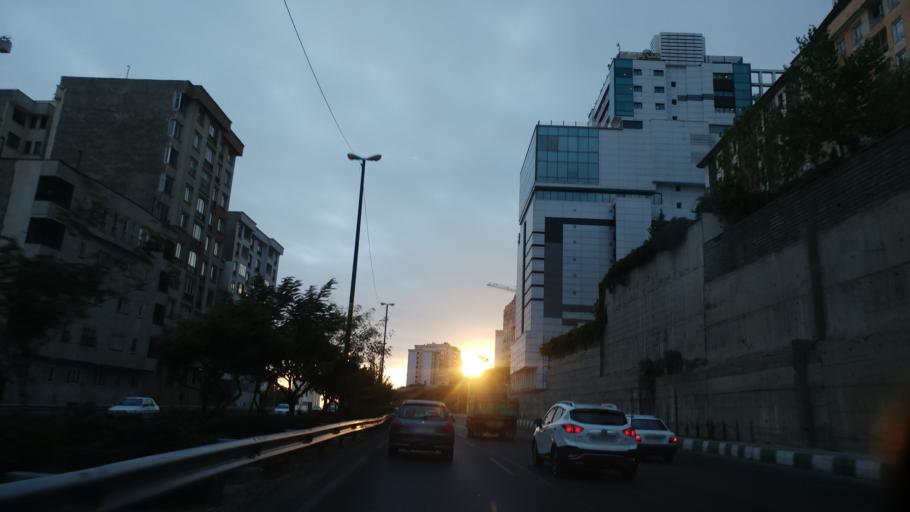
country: IR
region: Tehran
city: Tajrish
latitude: 35.7883
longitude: 51.3713
